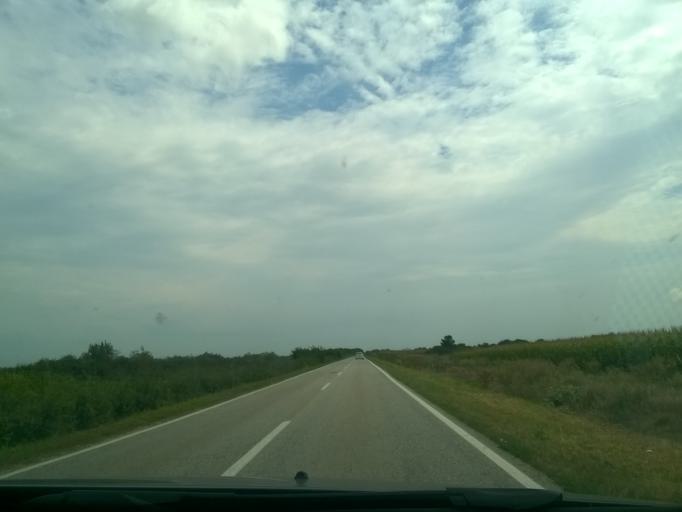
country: RS
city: Banatski Despotovac
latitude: 45.3875
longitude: 20.6174
